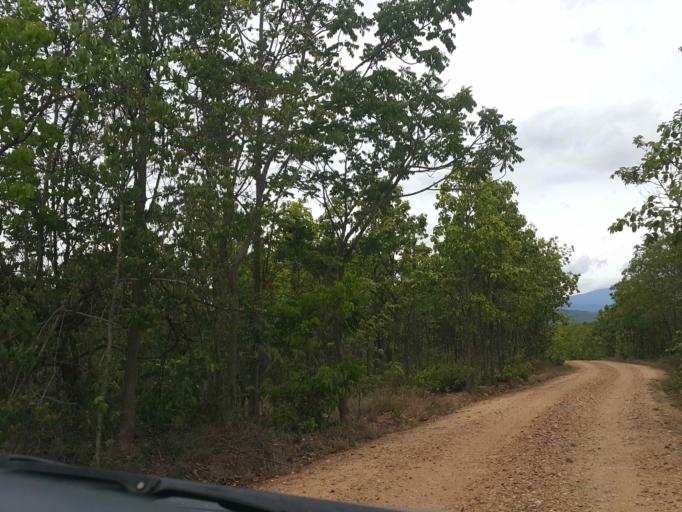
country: TH
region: Chiang Mai
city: Doi Lo
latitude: 18.5041
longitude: 98.7533
